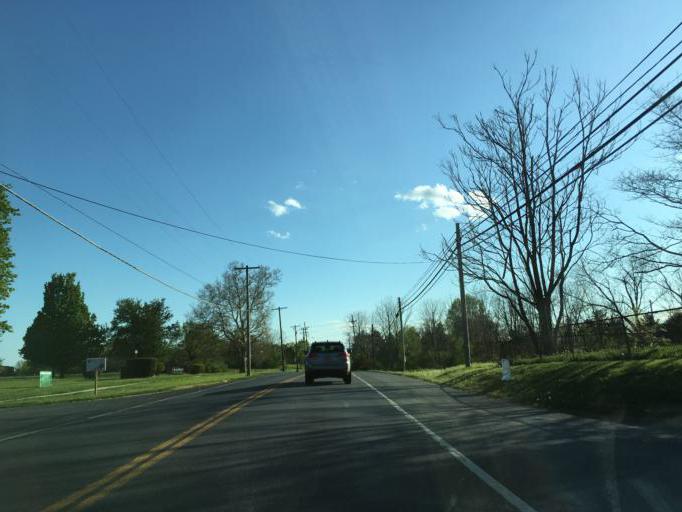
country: US
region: Maryland
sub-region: Frederick County
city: Frederick
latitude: 39.4374
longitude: -77.4012
